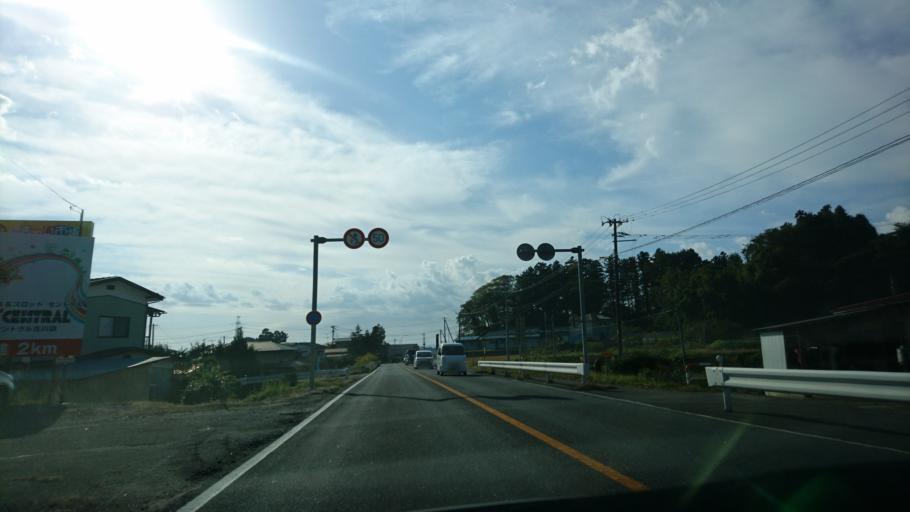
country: JP
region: Miyagi
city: Furukawa
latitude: 38.6228
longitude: 140.9836
